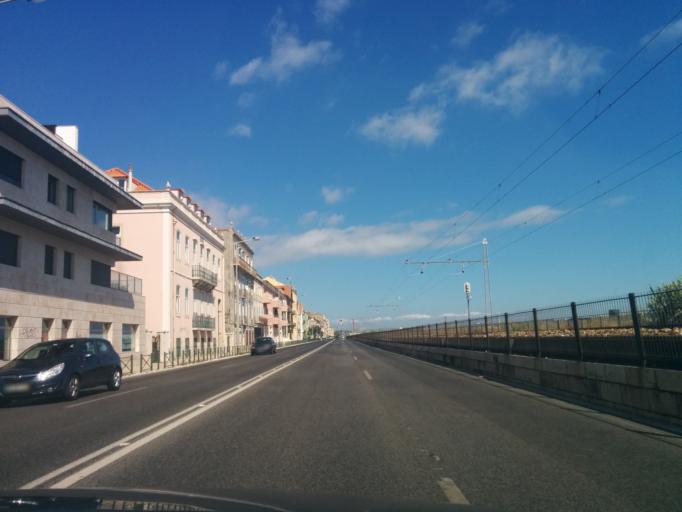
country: PT
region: Lisbon
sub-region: Oeiras
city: Linda-a-Velha
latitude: 38.6996
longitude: -9.2470
